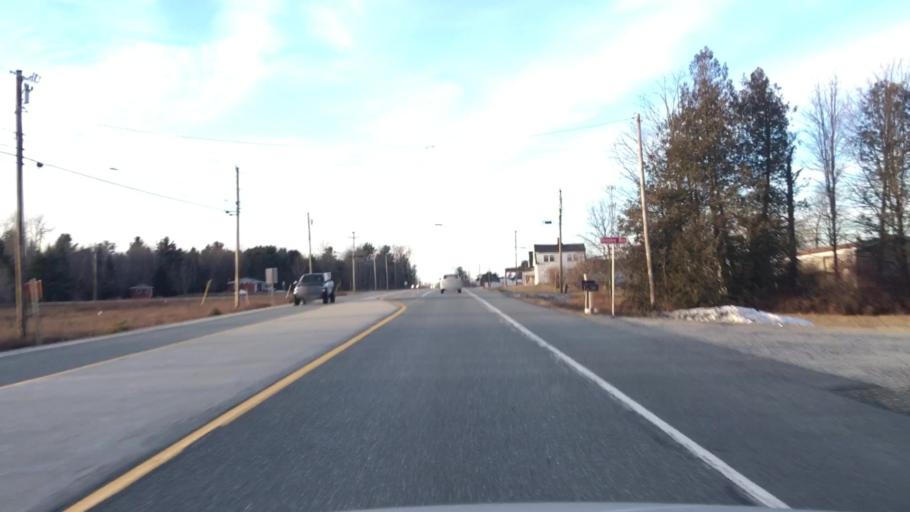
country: US
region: Maine
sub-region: Hancock County
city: Surry
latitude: 44.6146
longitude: -68.5241
